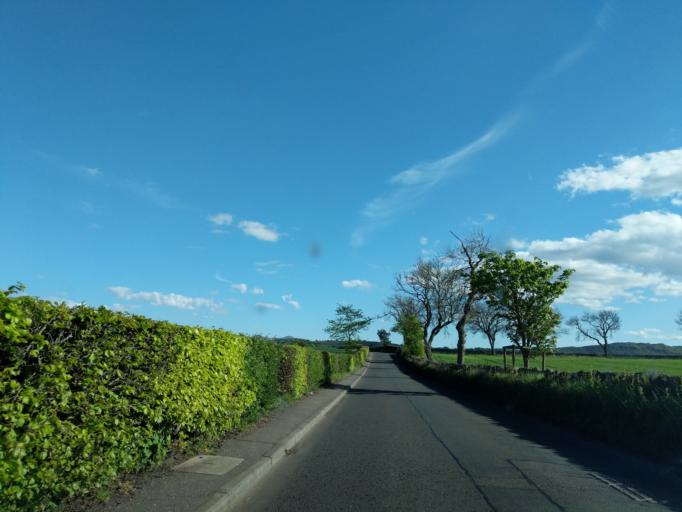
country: GB
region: Scotland
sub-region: Edinburgh
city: Ratho
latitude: 55.9134
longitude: -3.3734
